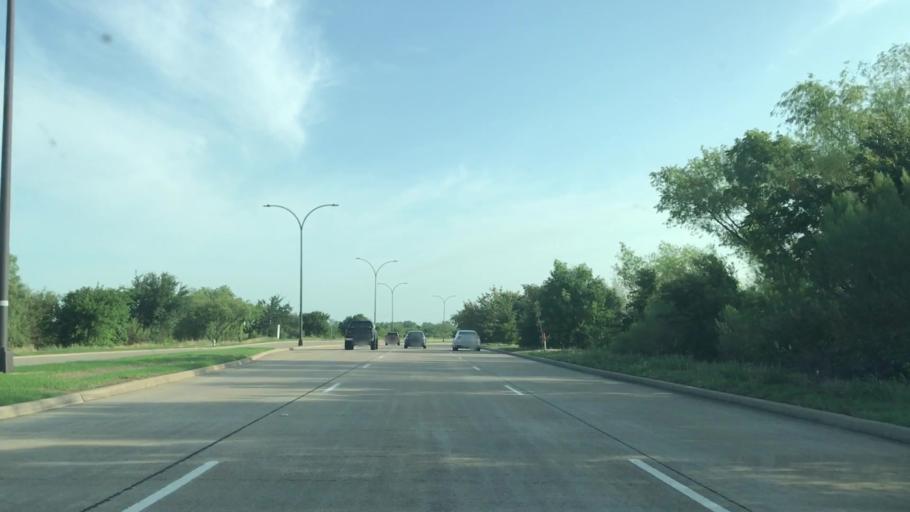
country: US
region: Texas
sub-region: Tarrant County
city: Arlington
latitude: 32.7753
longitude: -97.1363
